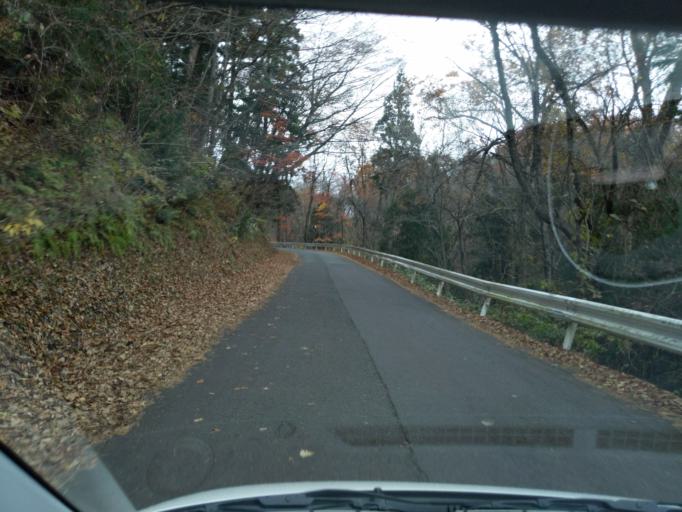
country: JP
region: Iwate
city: Ichinoseki
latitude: 38.9817
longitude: 141.0030
